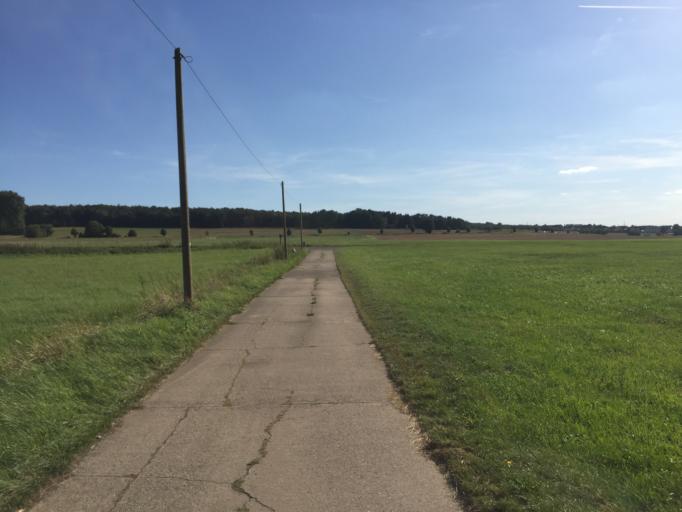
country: DE
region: Hesse
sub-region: Regierungsbezirk Giessen
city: Langgons
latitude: 50.5361
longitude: 8.6947
